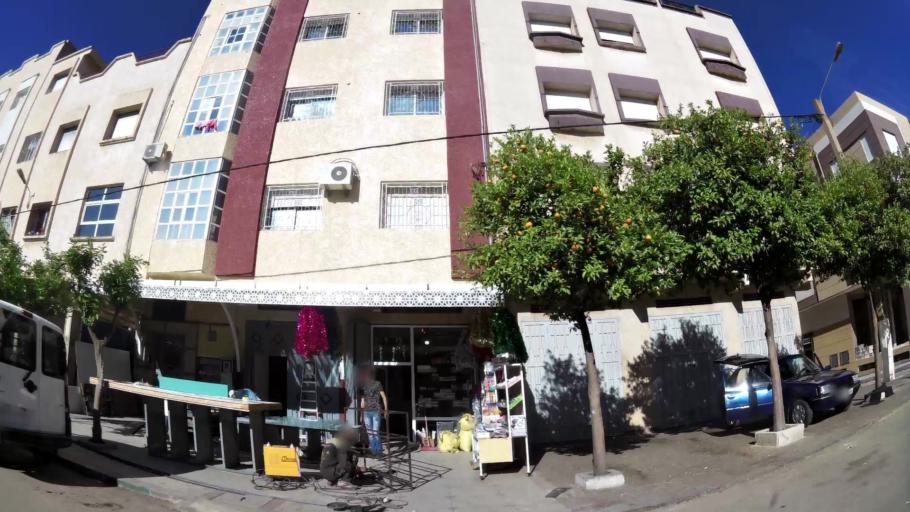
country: MA
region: Meknes-Tafilalet
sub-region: Meknes
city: Meknes
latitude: 33.8887
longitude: -5.4995
